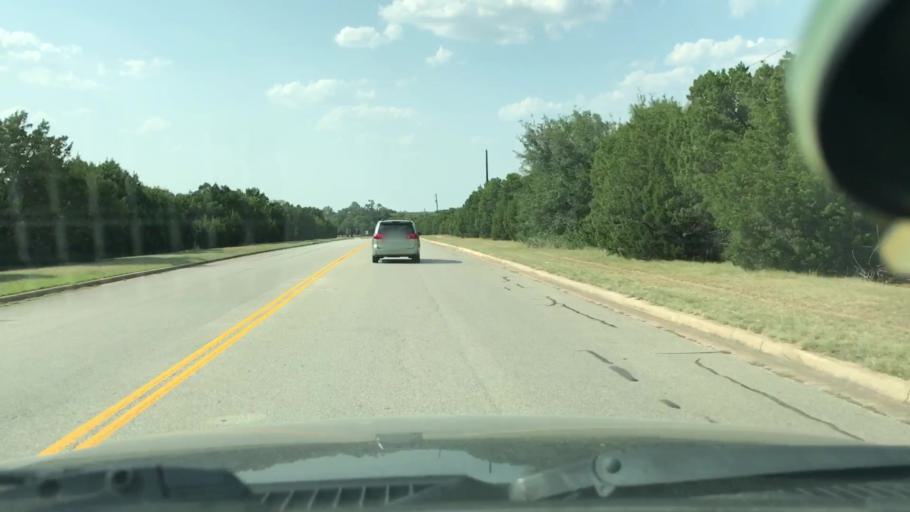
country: US
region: Texas
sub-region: Williamson County
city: Cedar Park
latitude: 30.5370
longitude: -97.8312
